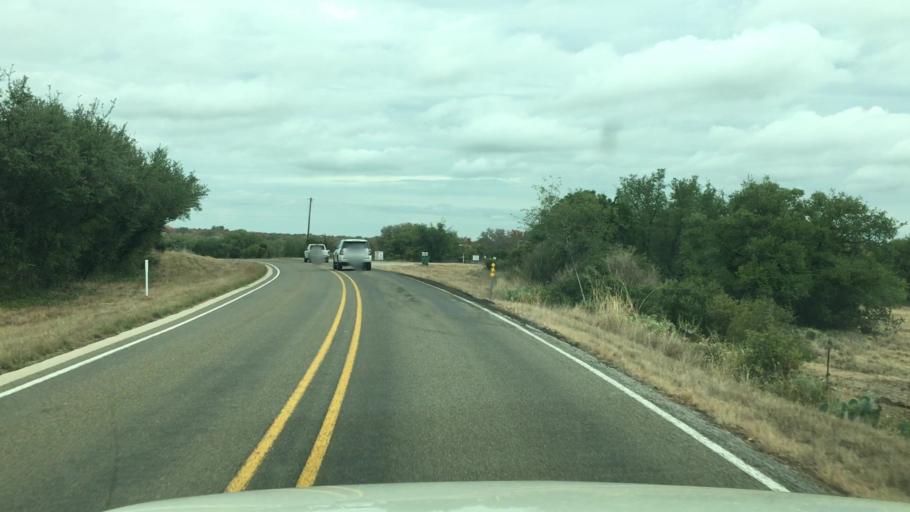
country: US
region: Texas
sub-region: Llano County
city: Horseshoe Bay
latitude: 30.4775
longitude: -98.4174
